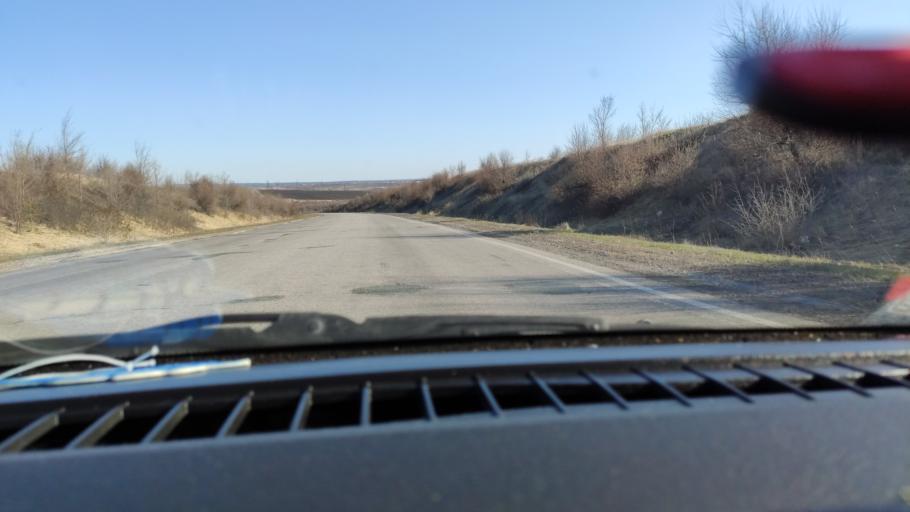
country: RU
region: Samara
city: Varlamovo
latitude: 53.0645
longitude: 48.3532
